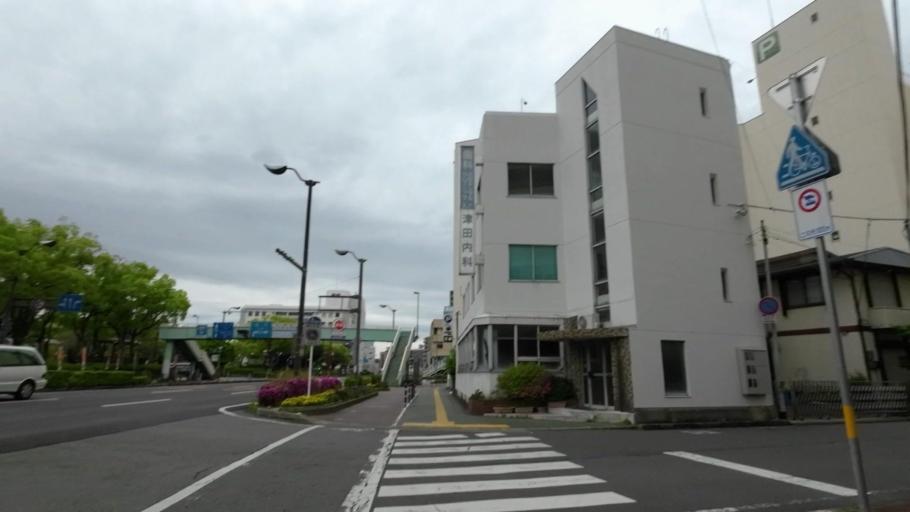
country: JP
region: Tokushima
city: Tokushima-shi
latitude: 34.0736
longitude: 134.5483
